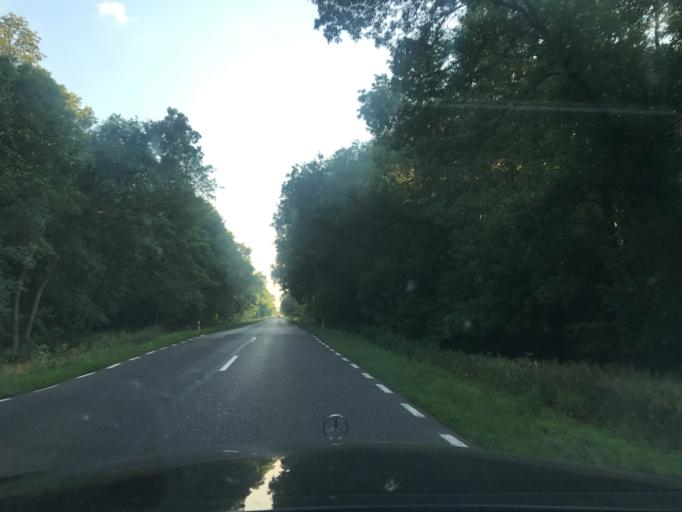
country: PL
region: Lublin Voivodeship
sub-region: Powiat parczewski
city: Debowa Kloda
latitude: 51.6650
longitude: 23.0097
